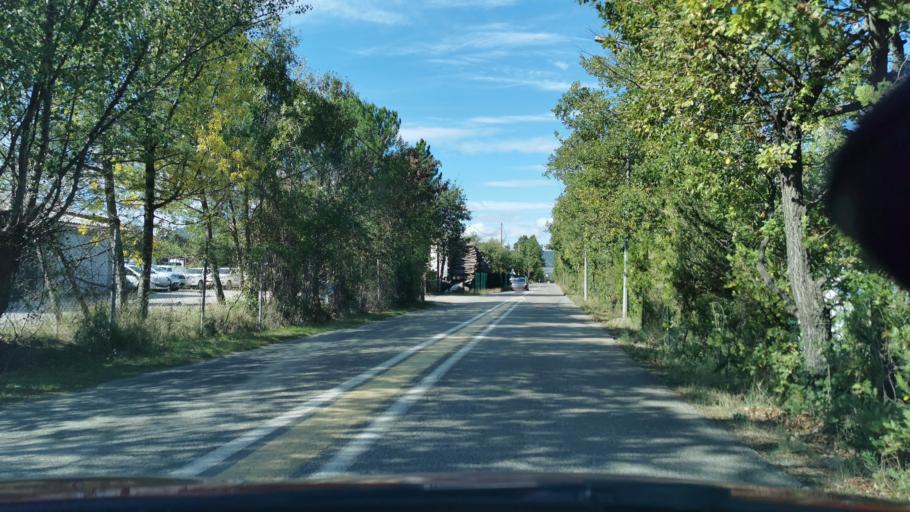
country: FR
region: Provence-Alpes-Cote d'Azur
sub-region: Departement des Alpes-de-Haute-Provence
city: Peipin
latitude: 44.1574
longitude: 5.9703
